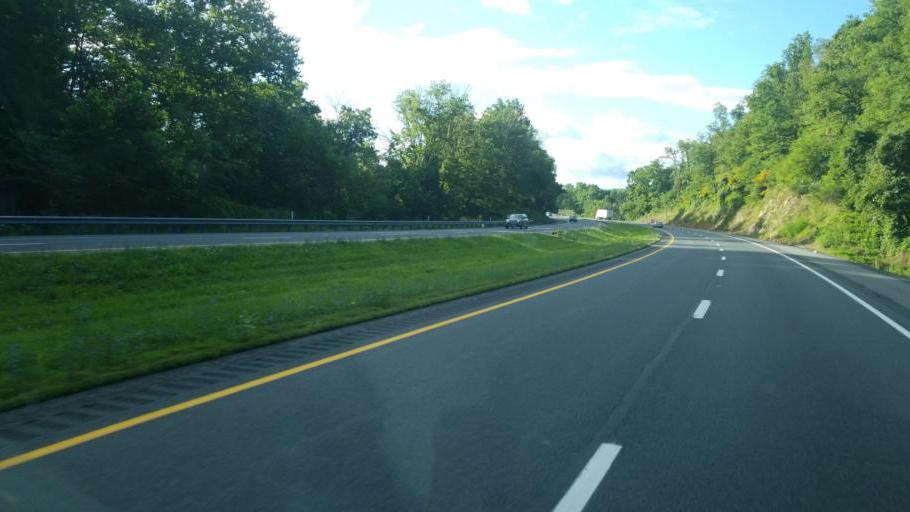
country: US
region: Maryland
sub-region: Washington County
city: Hancock
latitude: 39.7665
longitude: -78.2005
